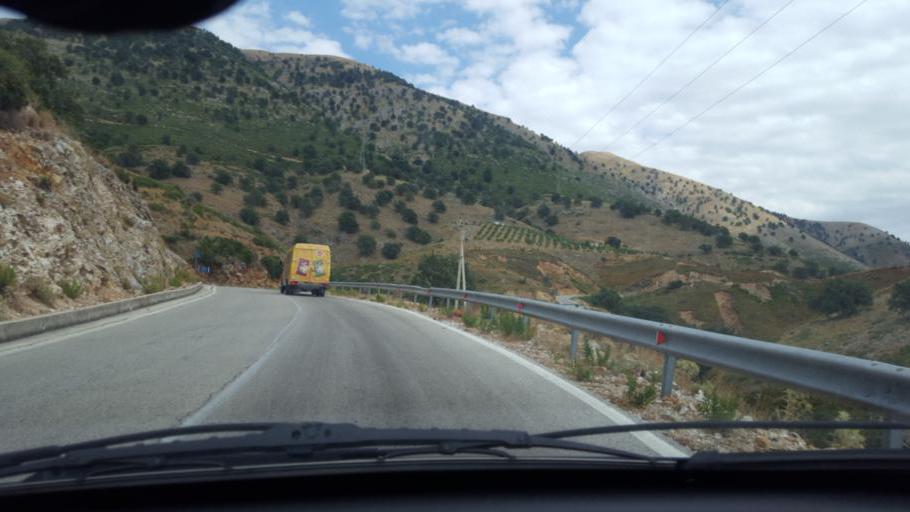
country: AL
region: Vlore
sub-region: Rrethi i Sarandes
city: Lukove
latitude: 40.0432
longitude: 19.8726
